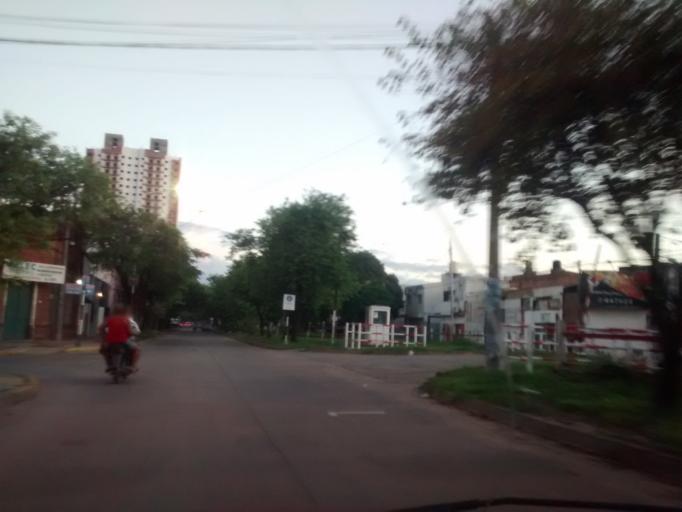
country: AR
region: Chaco
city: Resistencia
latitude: -27.4573
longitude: -58.9883
